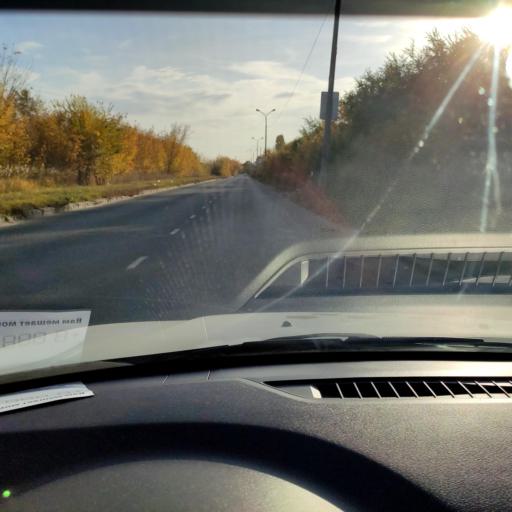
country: RU
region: Samara
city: Tol'yatti
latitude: 53.5553
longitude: 49.3116
